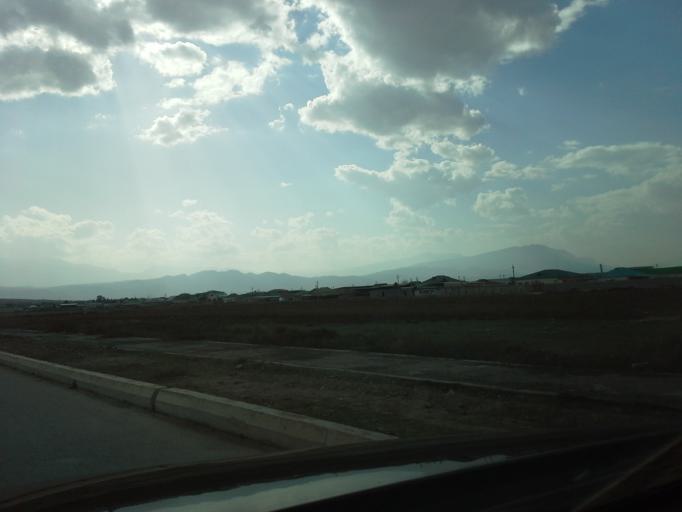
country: TM
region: Ahal
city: Ashgabat
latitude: 37.9898
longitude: 58.2993
